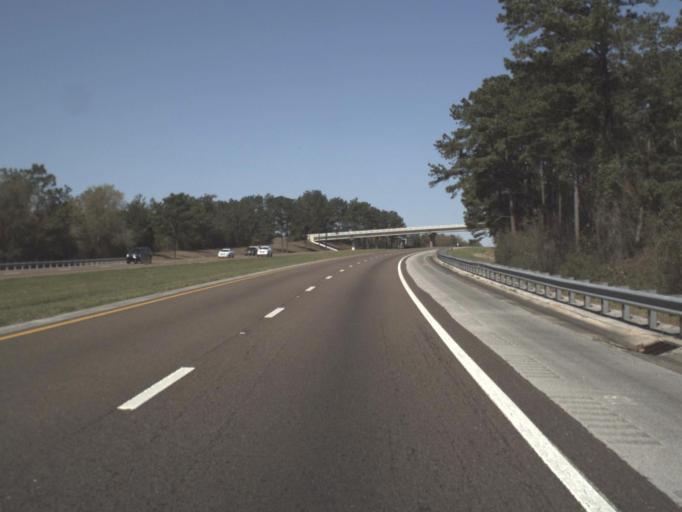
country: US
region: Florida
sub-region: Walton County
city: DeFuniak Springs
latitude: 30.7261
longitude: -86.2079
